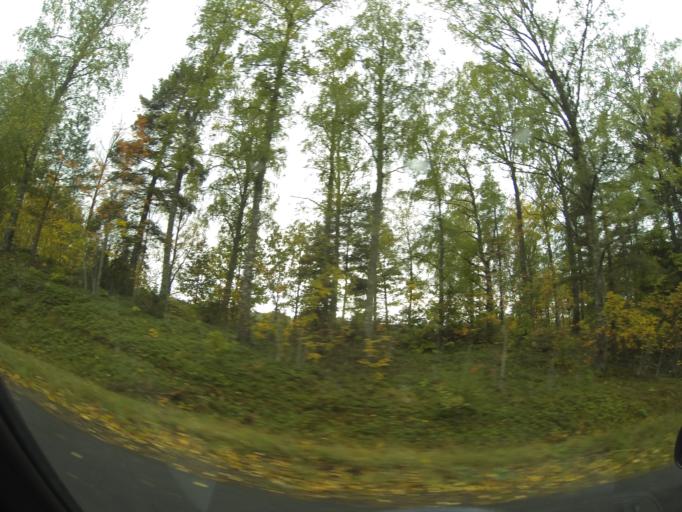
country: SE
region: Soedermanland
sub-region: Eskilstuna Kommun
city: Kvicksund
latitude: 59.3249
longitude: 16.3021
